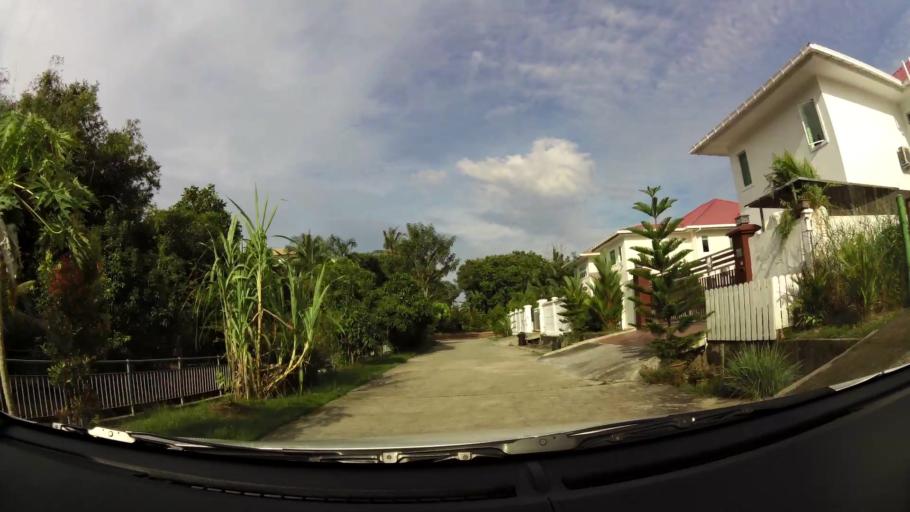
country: BN
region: Brunei and Muara
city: Bandar Seri Begawan
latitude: 4.9117
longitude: 114.8919
